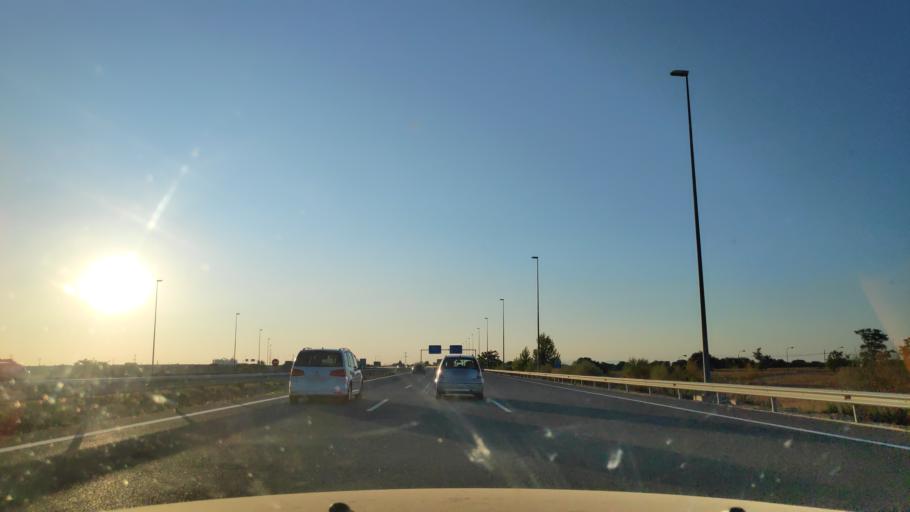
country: ES
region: Madrid
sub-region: Provincia de Madrid
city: Perales de Tajuna
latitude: 40.2642
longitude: -3.3875
